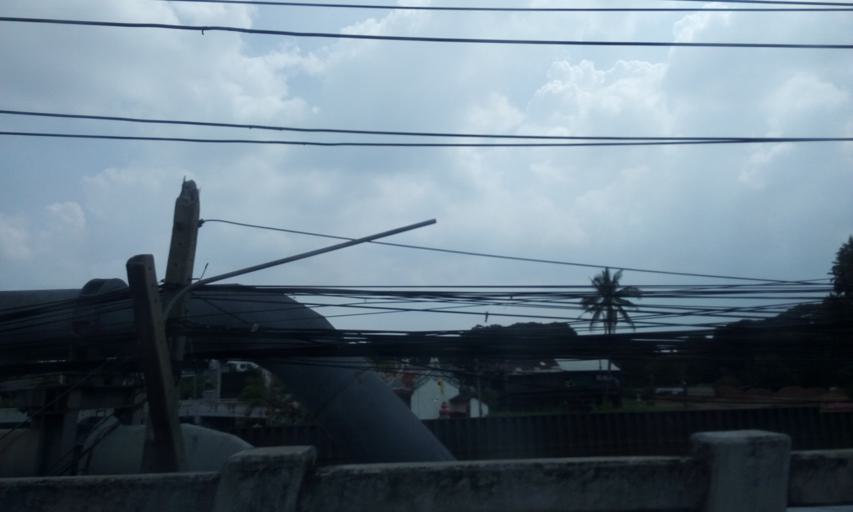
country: TH
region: Bangkok
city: Sai Mai
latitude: 13.9851
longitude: 100.6204
